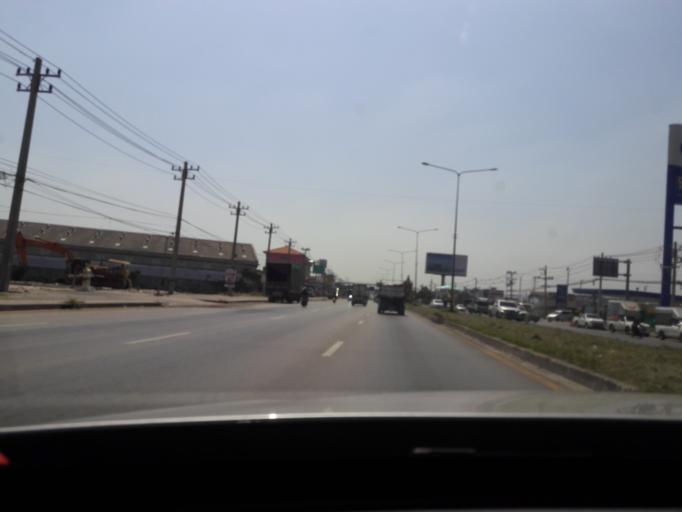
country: TH
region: Bangkok
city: Nong Khaem
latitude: 13.6781
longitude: 100.3201
